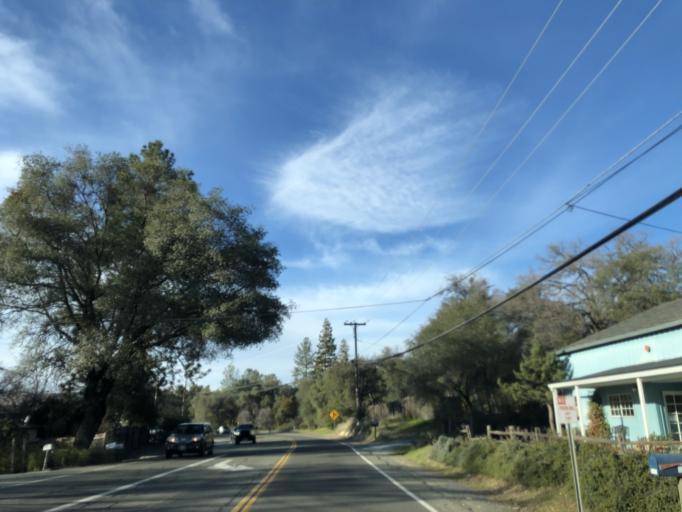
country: US
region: California
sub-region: El Dorado County
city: Diamond Springs
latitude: 38.7149
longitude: -120.8431
